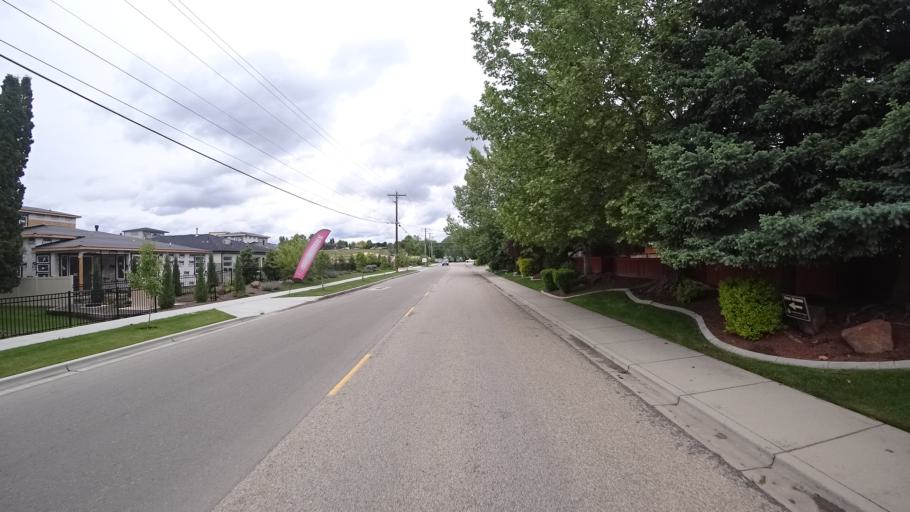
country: US
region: Idaho
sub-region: Ada County
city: Eagle
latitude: 43.6938
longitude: -116.3341
